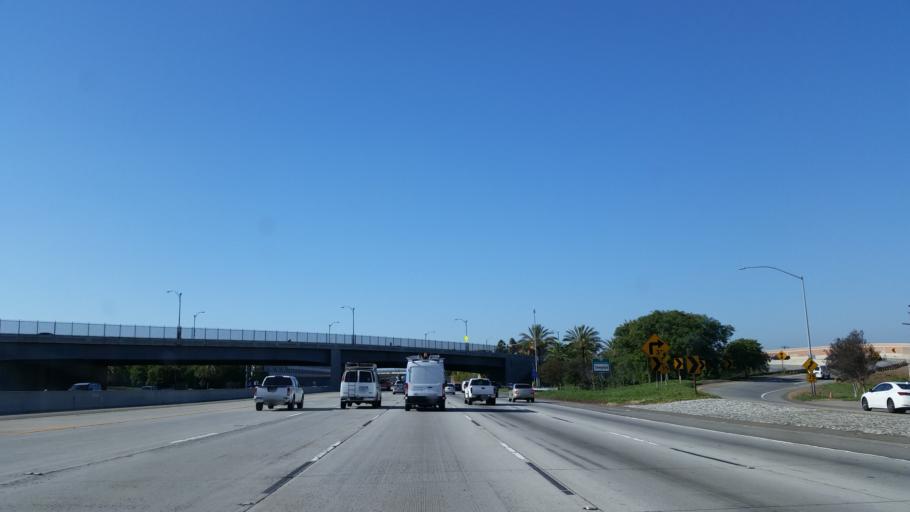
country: US
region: California
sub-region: Orange County
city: Anaheim
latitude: 33.8142
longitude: -117.9138
